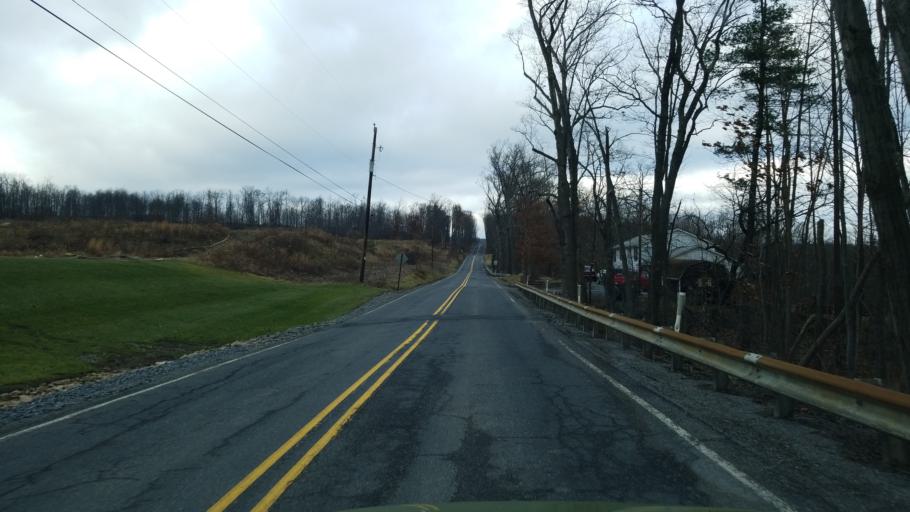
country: US
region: Pennsylvania
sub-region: Clearfield County
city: Hyde
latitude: 41.0440
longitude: -78.4892
